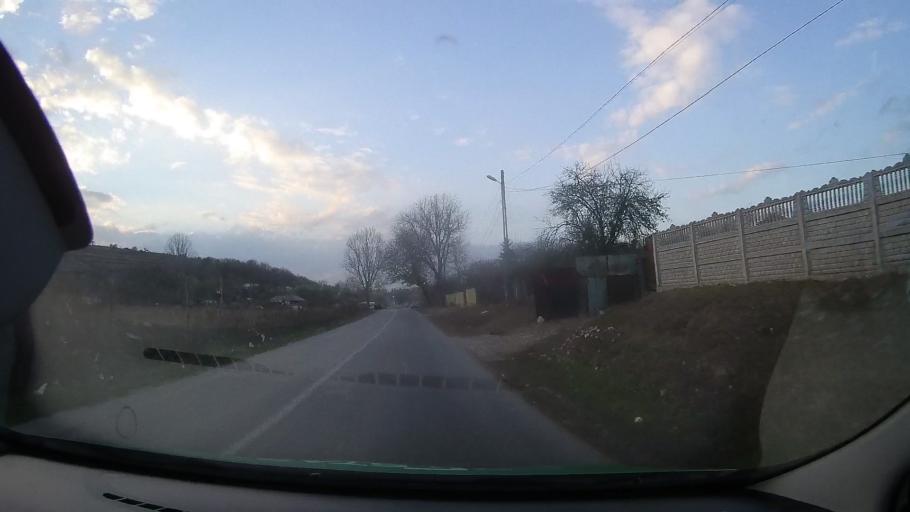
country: RO
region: Constanta
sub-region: Comuna Baneasa
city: Baneasa
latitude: 44.0601
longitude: 27.7085
